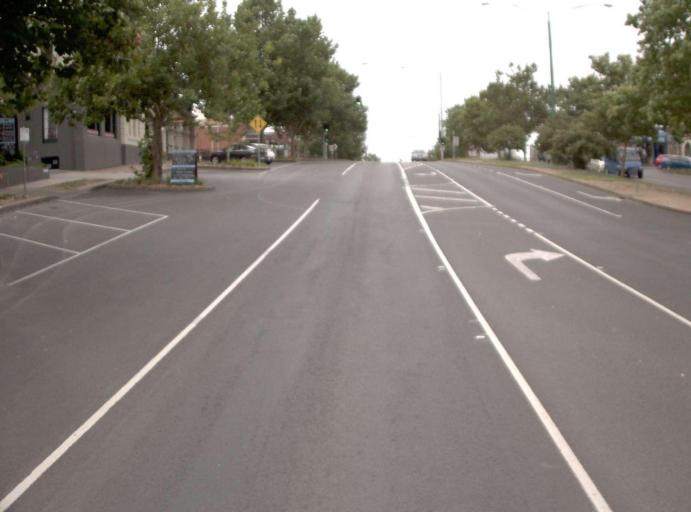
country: AU
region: Victoria
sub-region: Yarra Ranges
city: Yarra Glen
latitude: -37.6593
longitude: 145.3741
